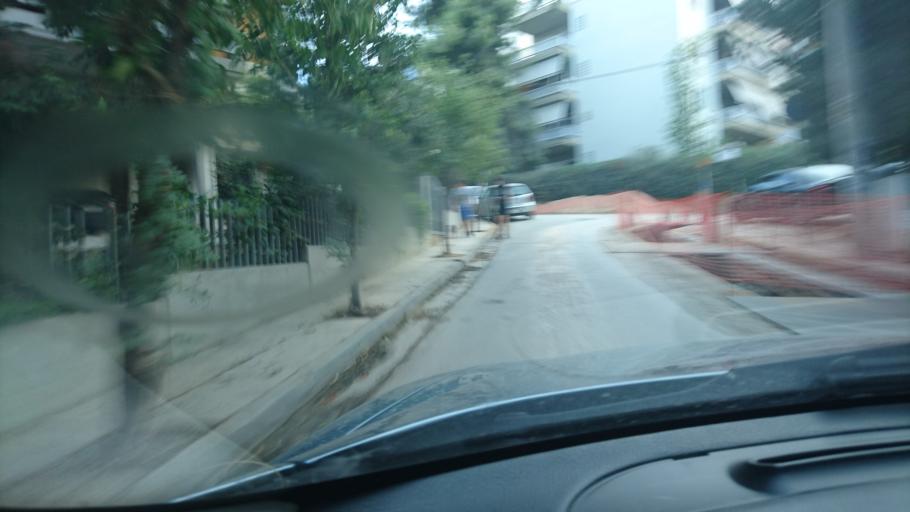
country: GR
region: Attica
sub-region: Nomarchia Athinas
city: Ilioupoli
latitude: 37.9459
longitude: 23.7675
